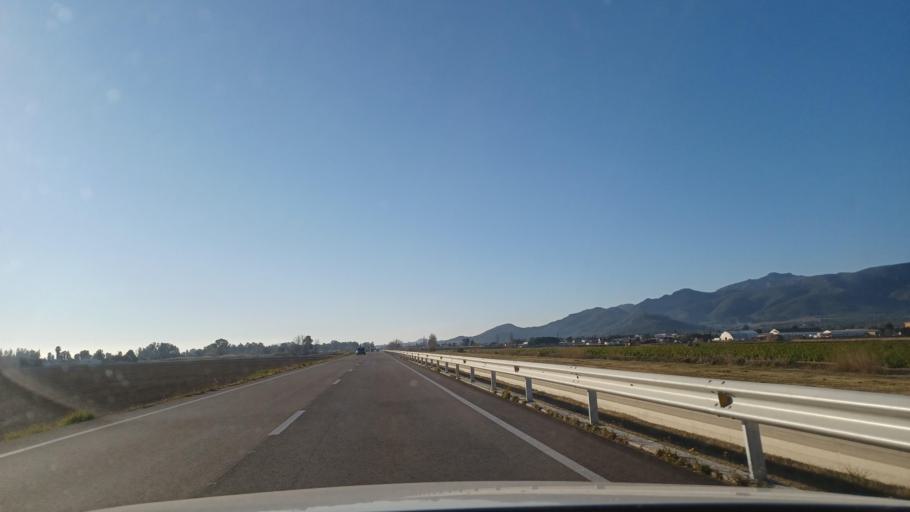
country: ES
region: Catalonia
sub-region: Provincia de Tarragona
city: Amposta
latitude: 40.6895
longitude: 0.5904
